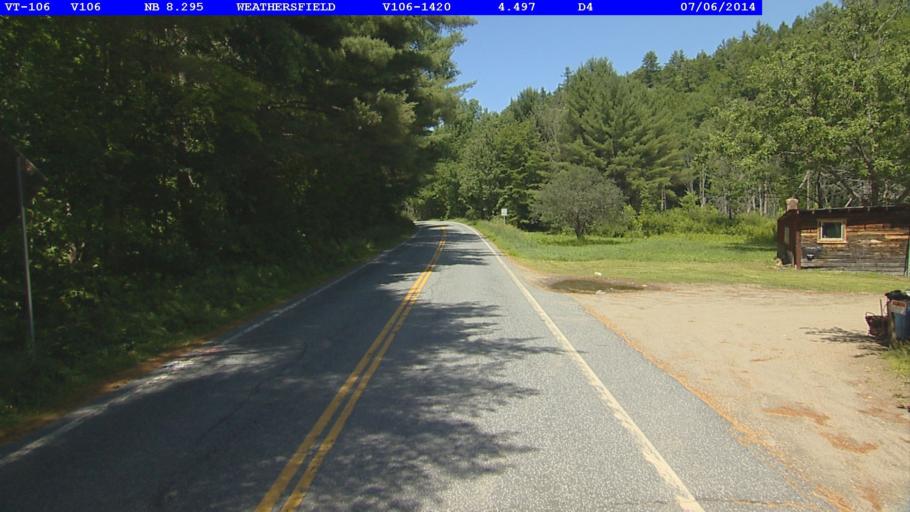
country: US
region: Vermont
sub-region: Windsor County
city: Springfield
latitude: 43.4031
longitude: -72.5143
